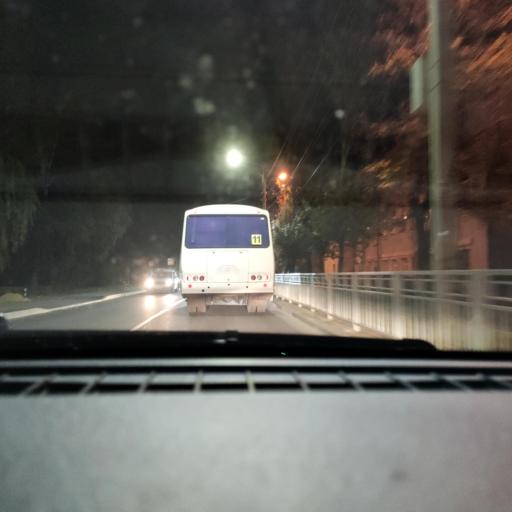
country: RU
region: Voronezj
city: Somovo
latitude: 51.7348
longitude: 39.2667
